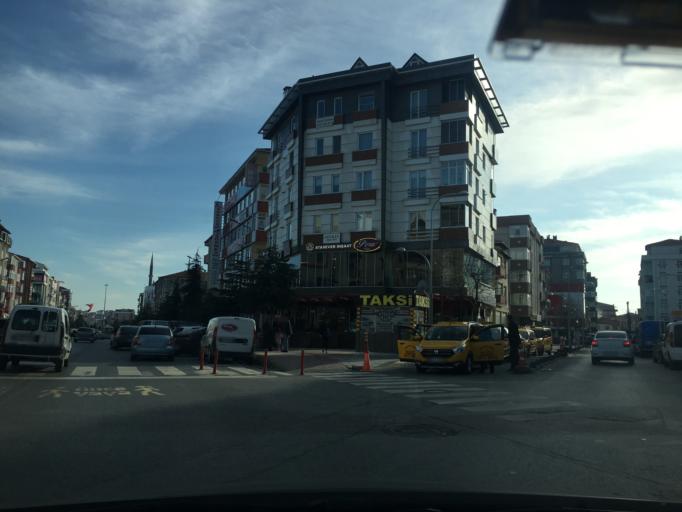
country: TR
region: Tekirdag
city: Cerkezkoey
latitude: 41.2900
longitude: 27.9986
